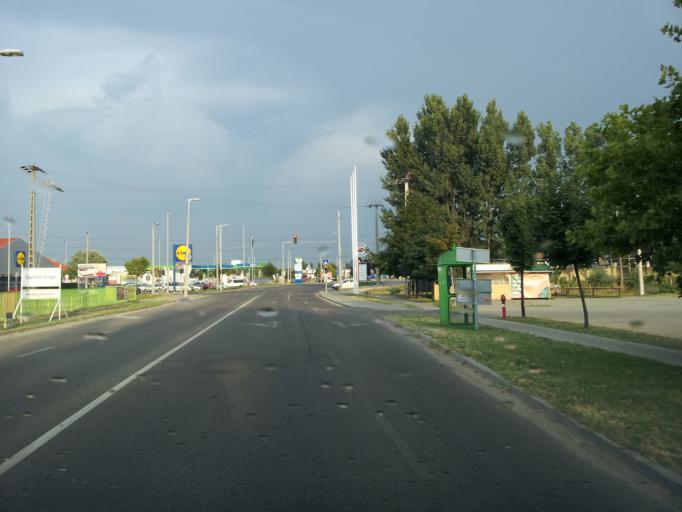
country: HU
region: Pest
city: Dunaharaszti
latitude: 47.3469
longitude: 19.1155
